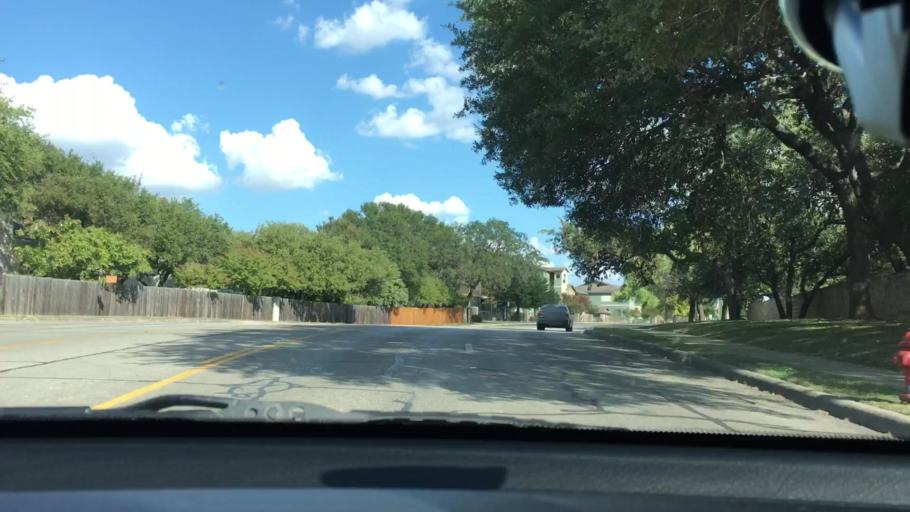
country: US
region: Texas
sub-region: Bexar County
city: Universal City
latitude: 29.5605
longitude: -98.3111
